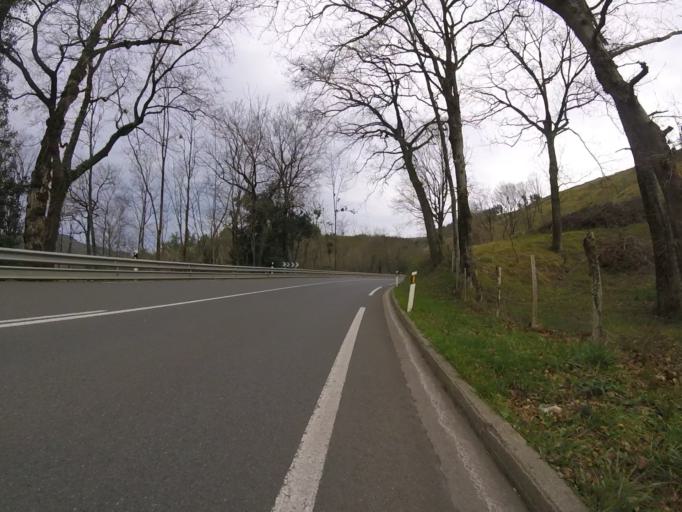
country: ES
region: Basque Country
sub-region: Provincia de Guipuzcoa
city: Aizarnazabal
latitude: 43.2770
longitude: -2.2262
